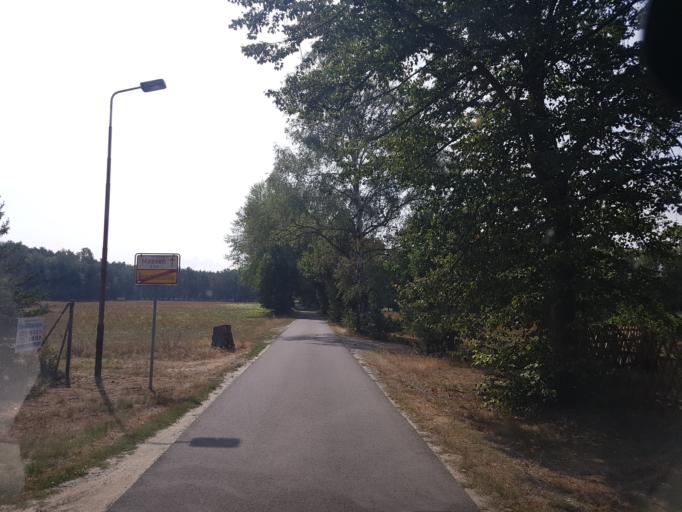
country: DE
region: Brandenburg
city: Finsterwalde
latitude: 51.6594
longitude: 13.7620
